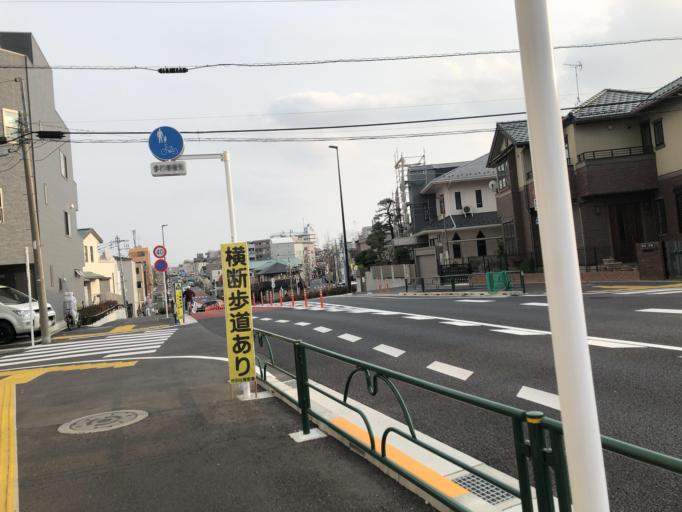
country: JP
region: Tokyo
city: Tokyo
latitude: 35.6441
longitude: 139.6423
